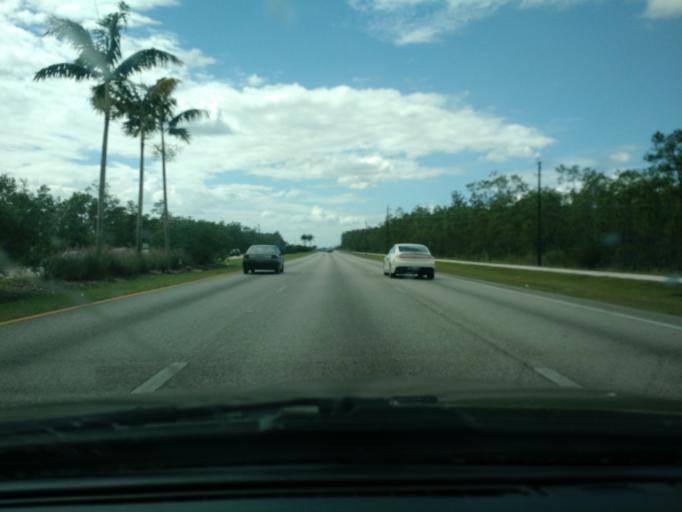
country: US
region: Florida
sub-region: Lee County
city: Gateway
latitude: 26.6131
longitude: -81.7864
